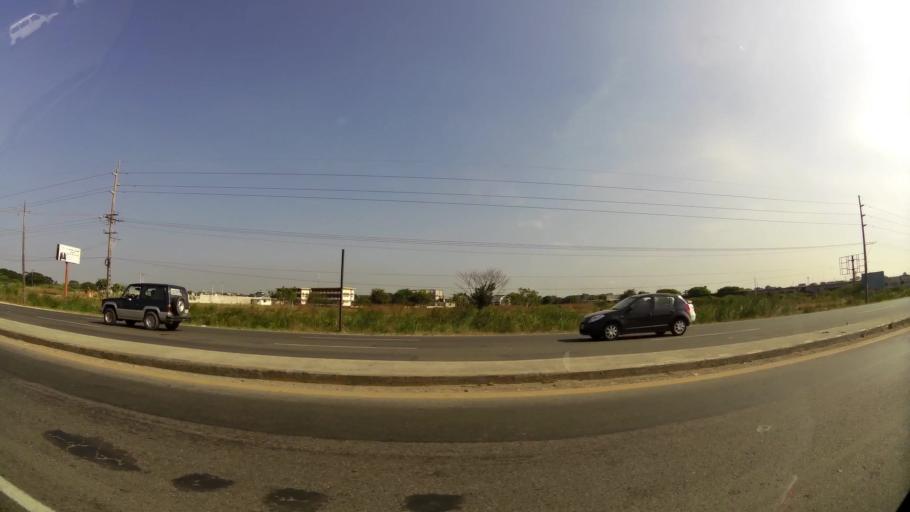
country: EC
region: Guayas
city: Eloy Alfaro
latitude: -2.1825
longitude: -79.8078
